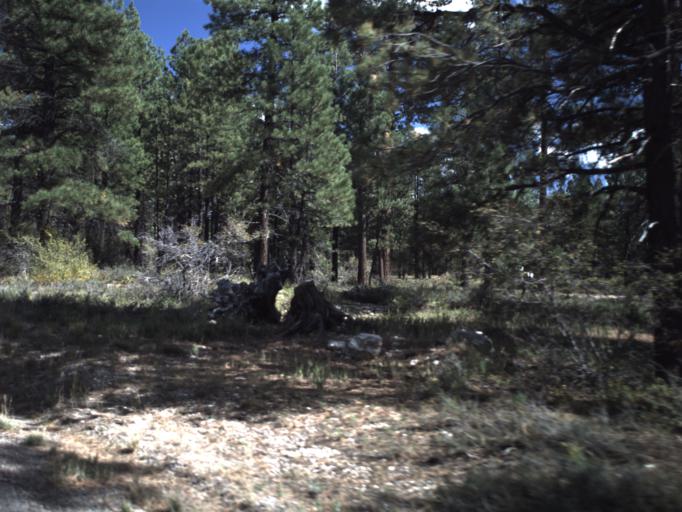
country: US
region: Utah
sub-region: Garfield County
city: Panguitch
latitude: 37.4913
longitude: -112.5651
